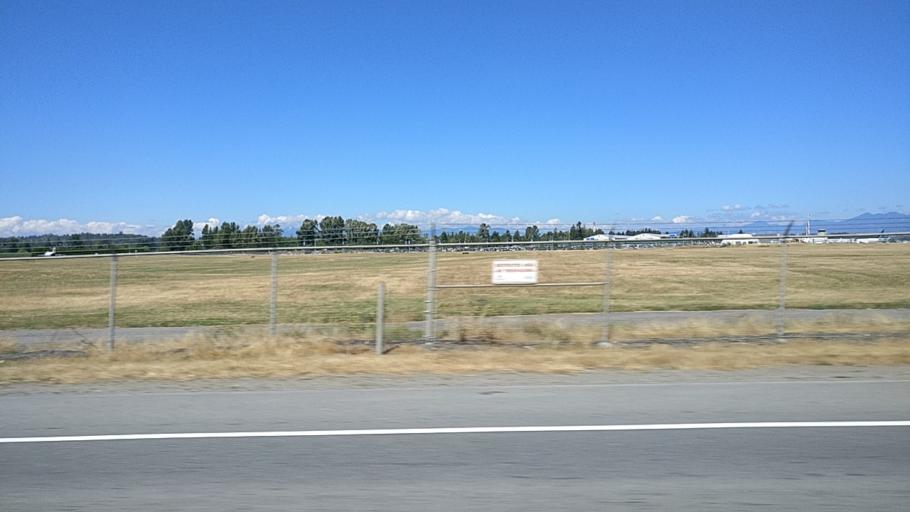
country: CA
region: British Columbia
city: Aldergrove
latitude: 49.0170
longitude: -122.3841
